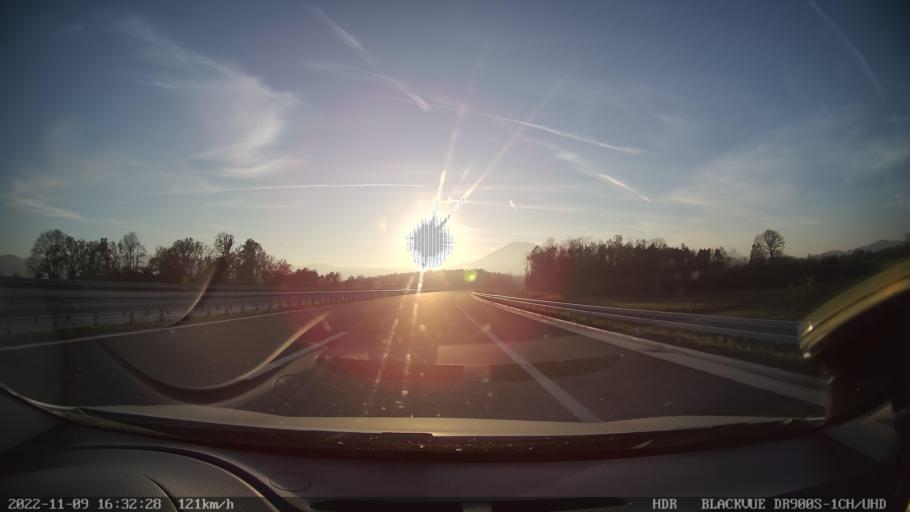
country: RS
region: Central Serbia
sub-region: Moravicki Okrug
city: Cacak
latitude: 43.9159
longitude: 20.2924
